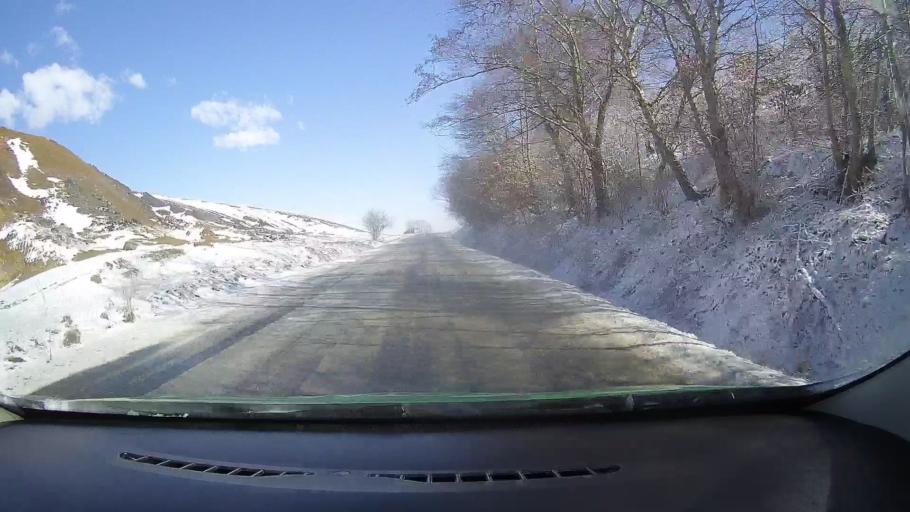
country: RO
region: Sibiu
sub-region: Comuna Rosia
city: Rosia
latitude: 45.7903
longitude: 24.3156
